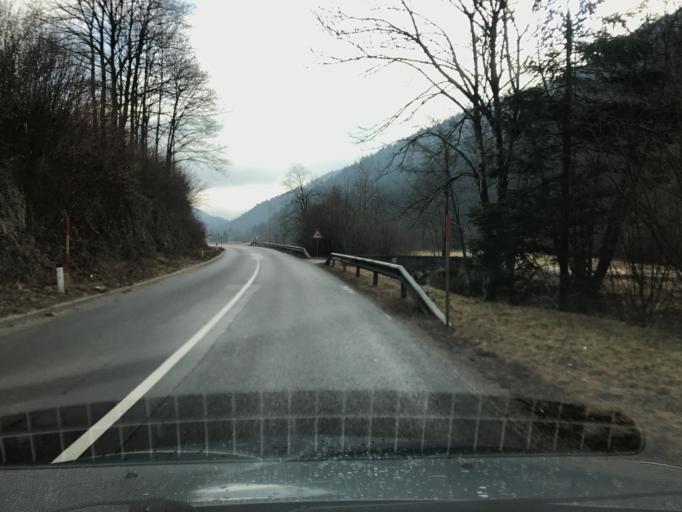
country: SI
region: Lukovica
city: Lukovica pri Domzalah
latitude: 46.2168
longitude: 14.7133
